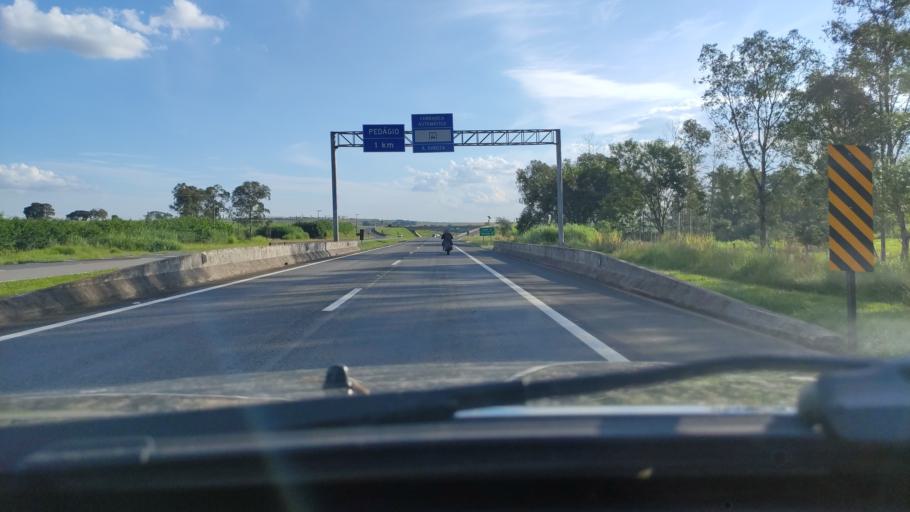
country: BR
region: Sao Paulo
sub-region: Mogi-Mirim
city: Mogi Mirim
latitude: -22.4534
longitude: -46.8931
